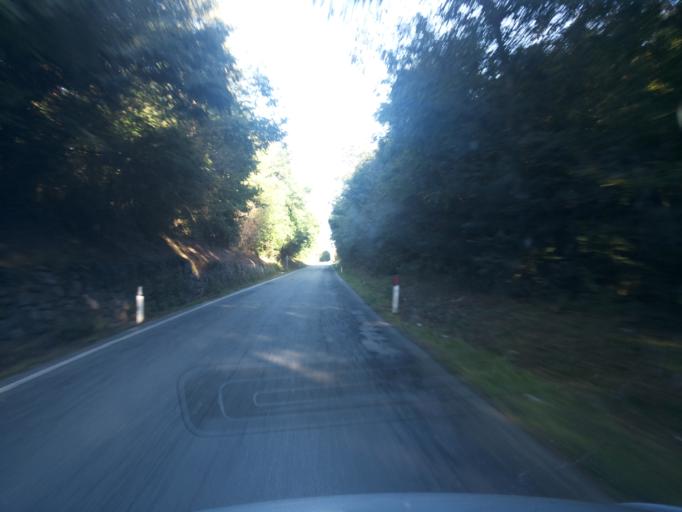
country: IT
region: Piedmont
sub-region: Provincia di Torino
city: Caravino
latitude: 45.3989
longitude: 7.9490
